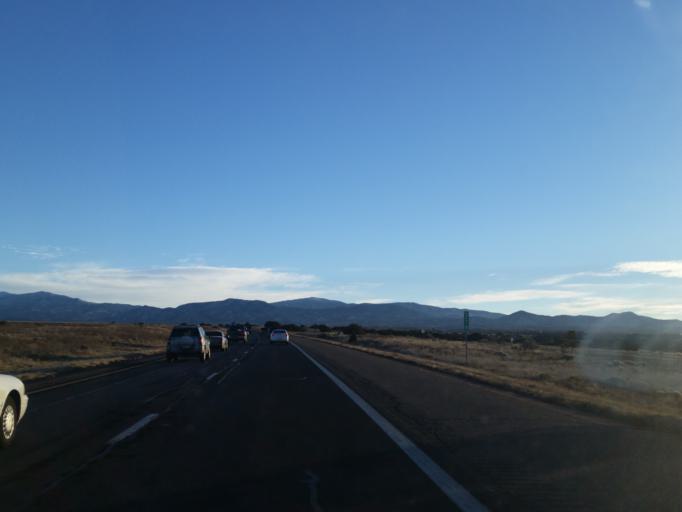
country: US
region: New Mexico
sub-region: Santa Fe County
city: Agua Fria
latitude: 35.6149
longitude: -106.0148
